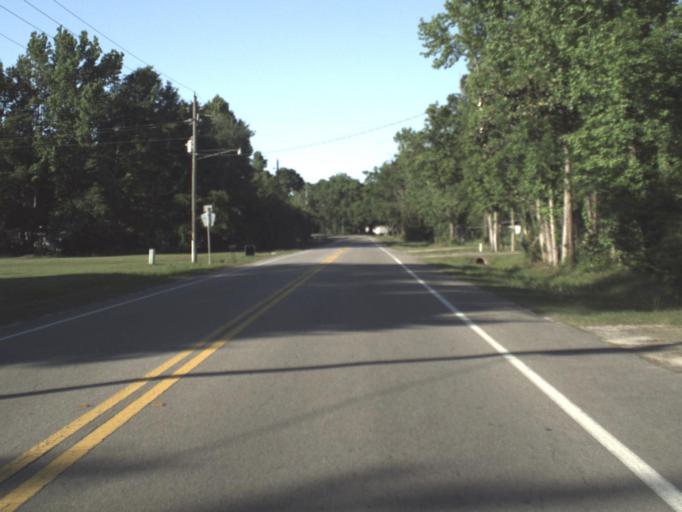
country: US
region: Florida
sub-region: Liberty County
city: Bristol
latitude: 30.3788
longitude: -84.8004
